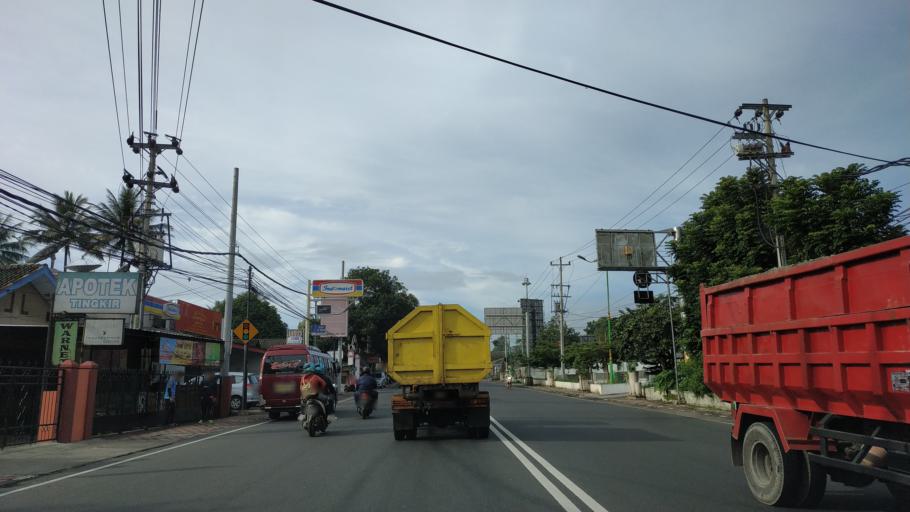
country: ID
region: Central Java
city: Salatiga
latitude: -7.3633
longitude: 110.5138
